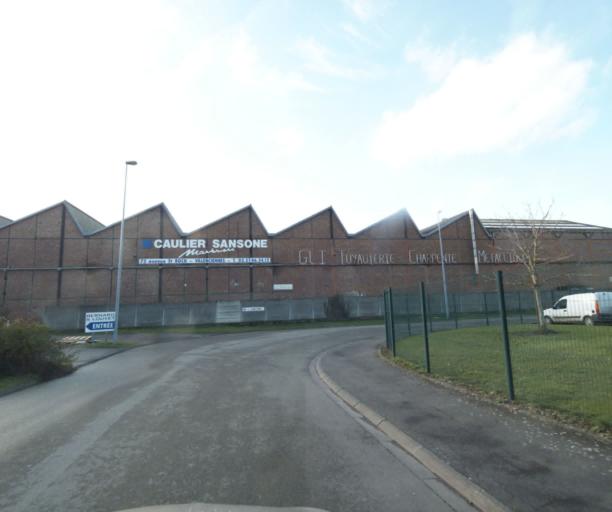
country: FR
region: Nord-Pas-de-Calais
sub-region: Departement du Nord
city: Marly
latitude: 50.3475
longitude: 3.5420
